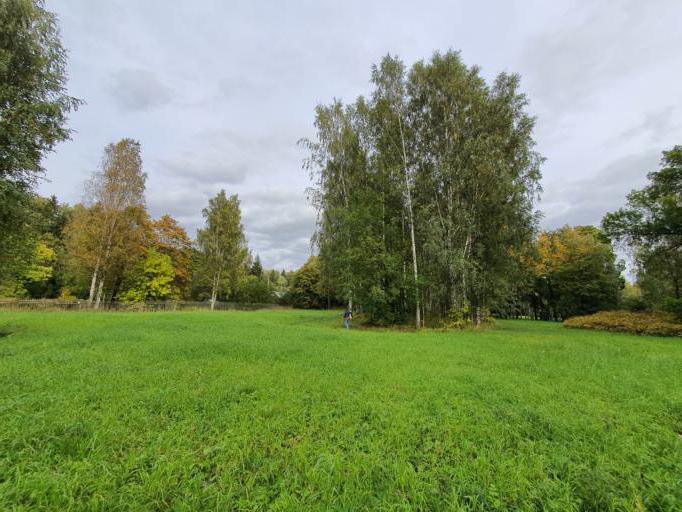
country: RU
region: St.-Petersburg
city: Pavlovsk
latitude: 59.6889
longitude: 30.4399
